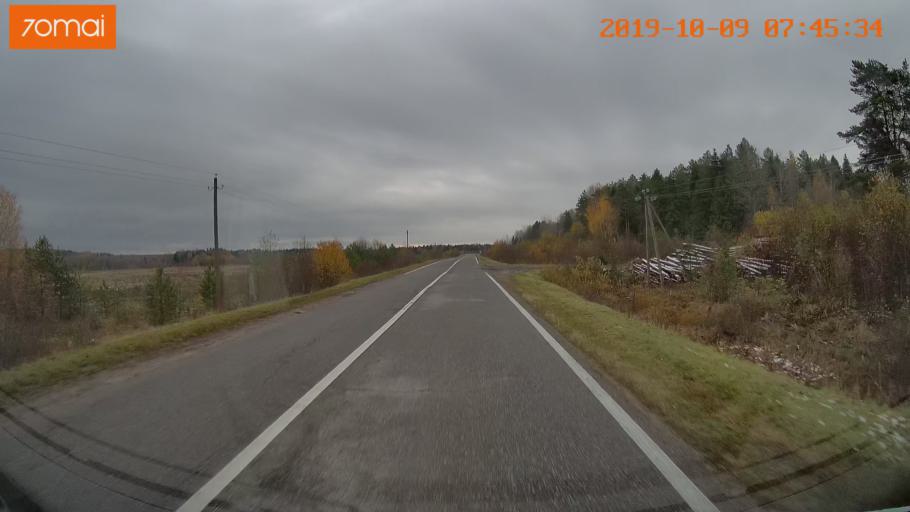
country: RU
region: Jaroslavl
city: Kukoboy
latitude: 58.6544
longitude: 39.7699
